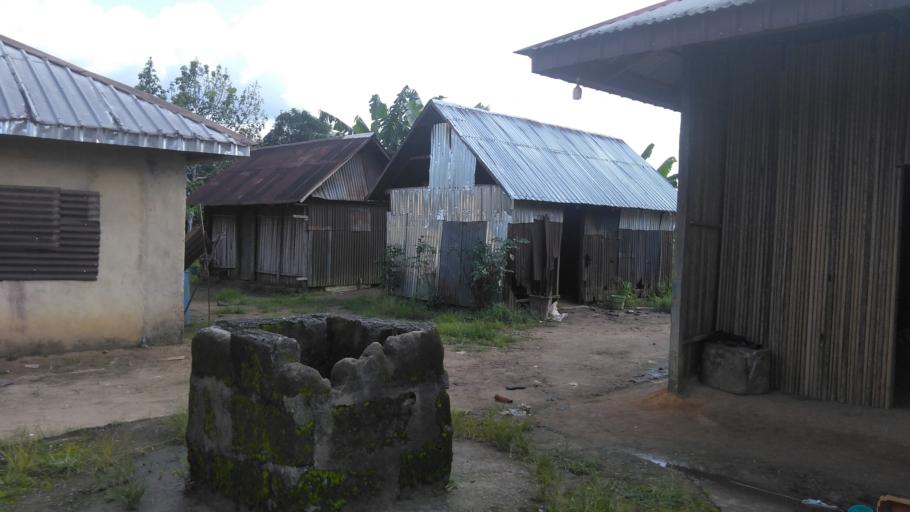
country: NG
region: Edo
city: Siluko
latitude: 6.1432
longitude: 5.2010
